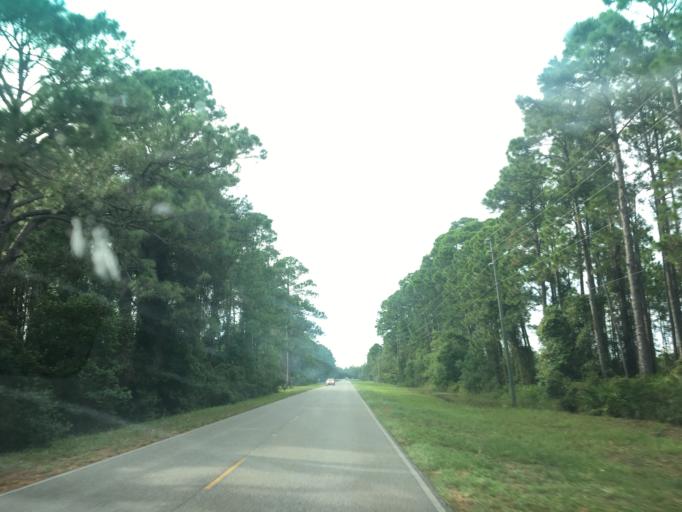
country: US
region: Florida
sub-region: Wakulla County
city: Crawfordville
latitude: 29.9392
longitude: -84.3825
